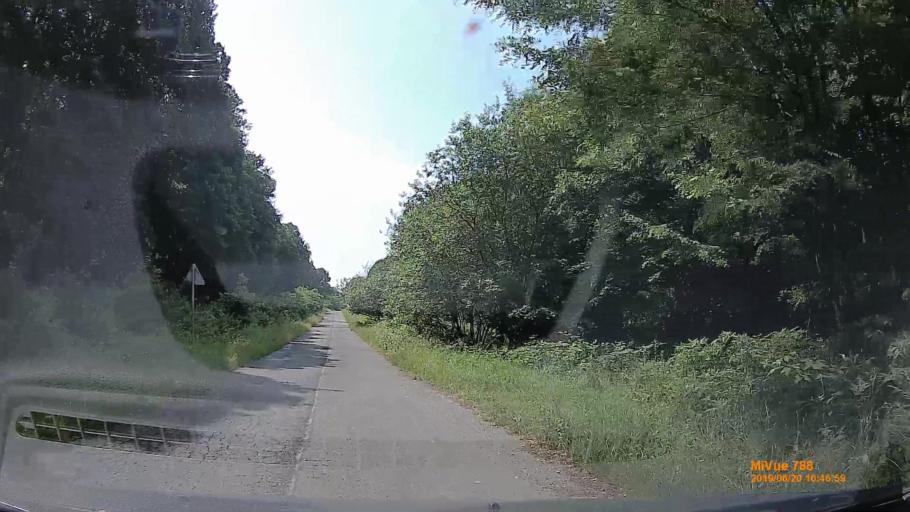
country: HU
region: Baranya
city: Hidas
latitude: 46.1780
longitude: 18.5816
